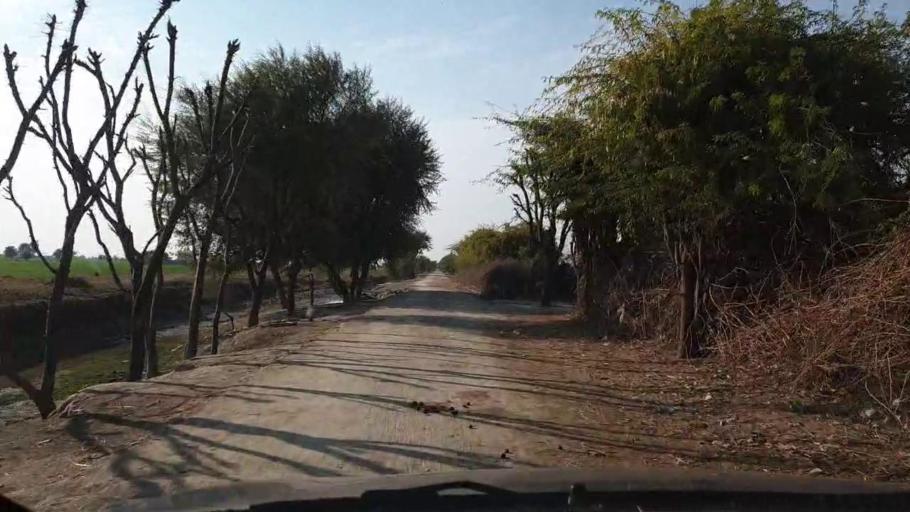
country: PK
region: Sindh
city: Sinjhoro
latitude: 25.9763
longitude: 68.8222
